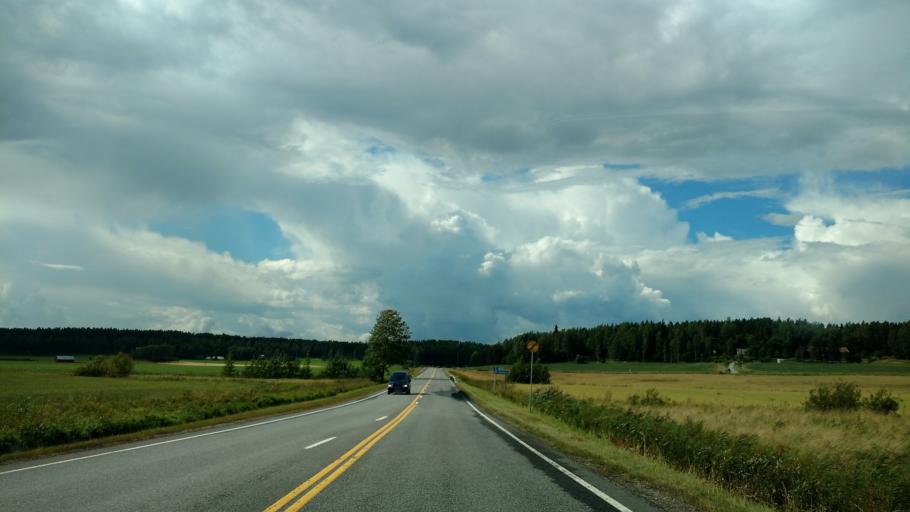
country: FI
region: Varsinais-Suomi
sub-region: Salo
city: Halikko
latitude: 60.3812
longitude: 22.9003
